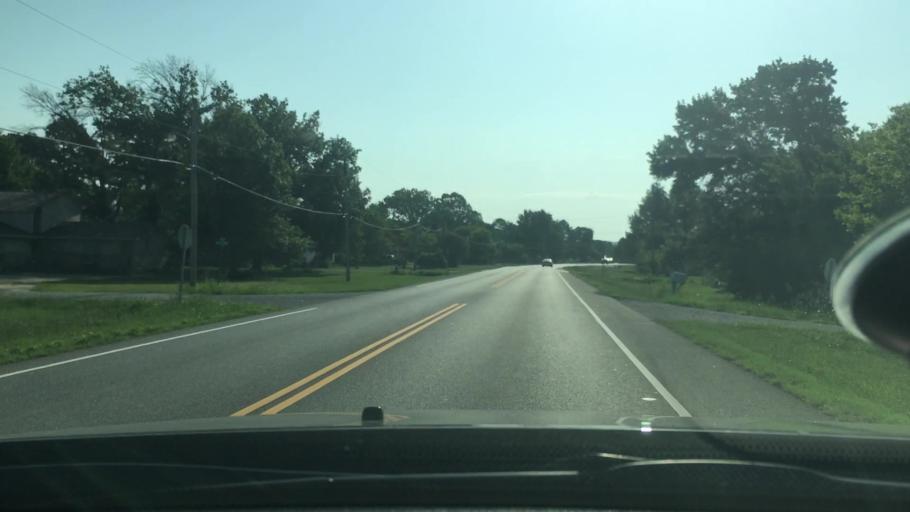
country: US
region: Oklahoma
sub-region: Atoka County
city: Atoka
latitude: 34.3944
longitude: -96.1392
